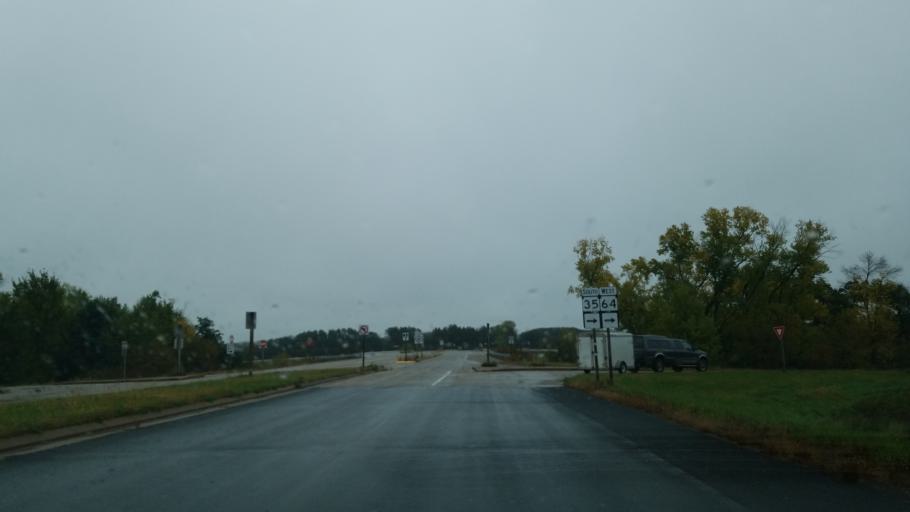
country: US
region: Minnesota
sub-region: Washington County
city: Stillwater
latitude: 45.0900
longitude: -92.7421
